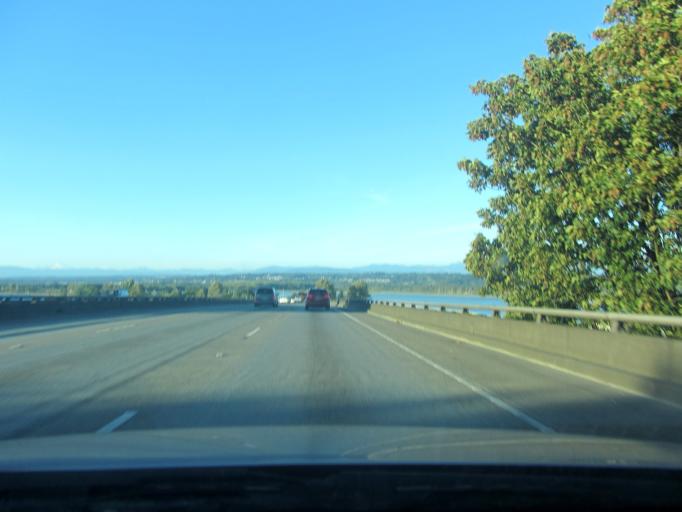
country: US
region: Washington
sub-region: Snohomish County
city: Everett
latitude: 47.9920
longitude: -122.1811
